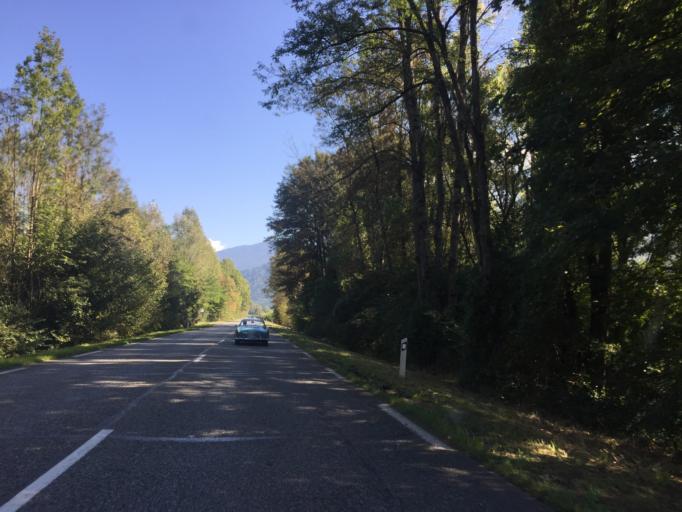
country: FR
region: Rhone-Alpes
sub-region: Departement de la Savoie
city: Aiton
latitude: 45.5789
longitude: 6.2553
